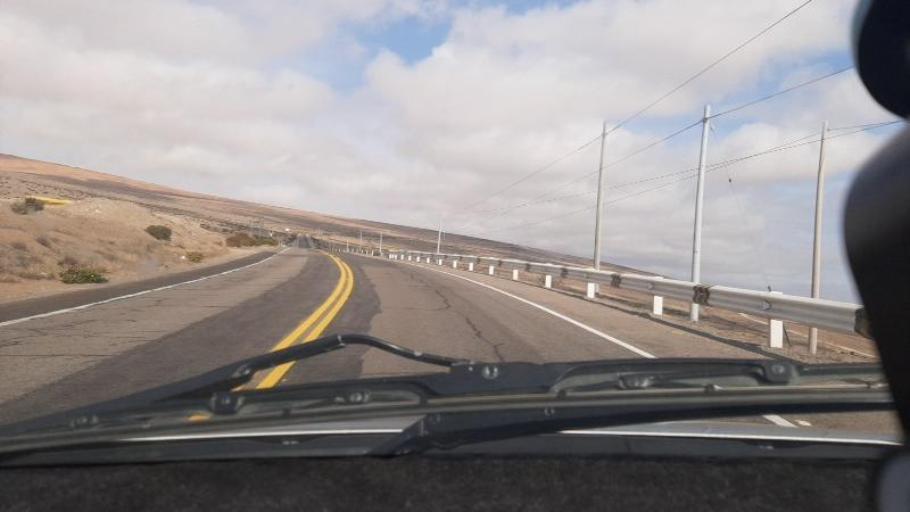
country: PE
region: Moquegua
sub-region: Provincia de Ilo
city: El Algarrobal
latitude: -17.6878
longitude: -71.2868
